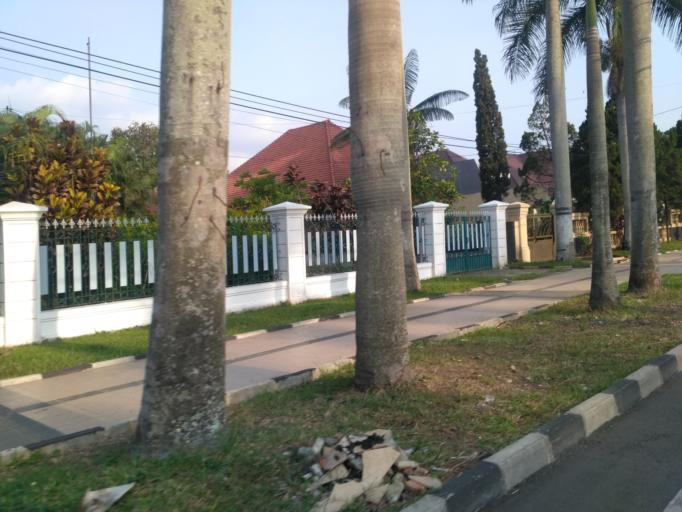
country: ID
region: East Java
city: Malang
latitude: -7.9701
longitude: 112.6229
